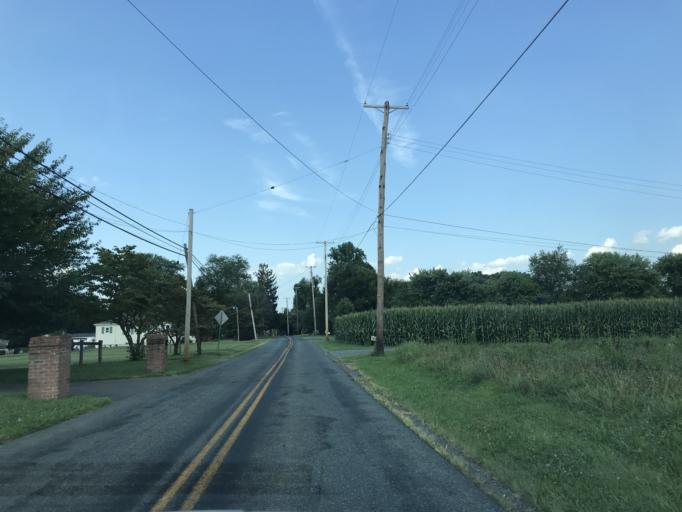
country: US
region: Maryland
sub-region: Harford County
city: South Bel Air
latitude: 39.6061
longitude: -76.3013
